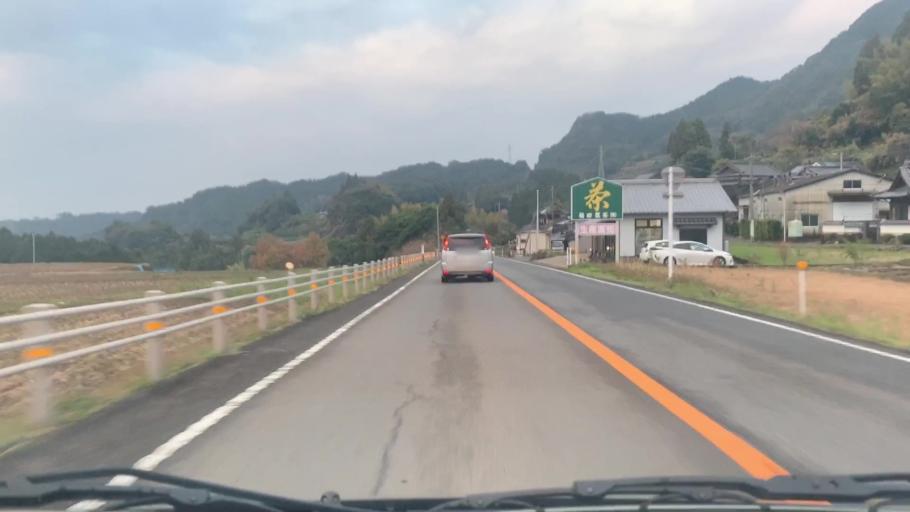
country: JP
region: Saga Prefecture
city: Ureshinomachi-shimojuku
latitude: 33.0596
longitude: 129.9527
